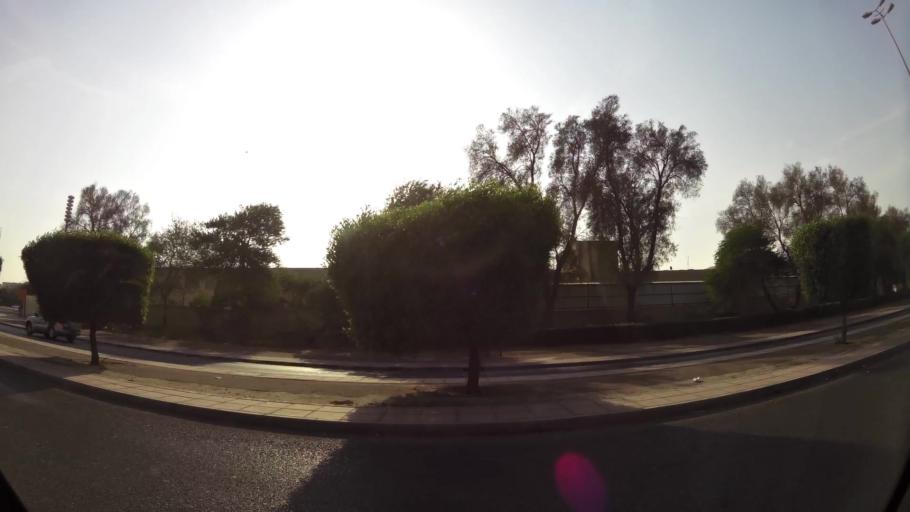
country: KW
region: Mubarak al Kabir
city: Mubarak al Kabir
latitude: 29.1721
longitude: 48.0778
